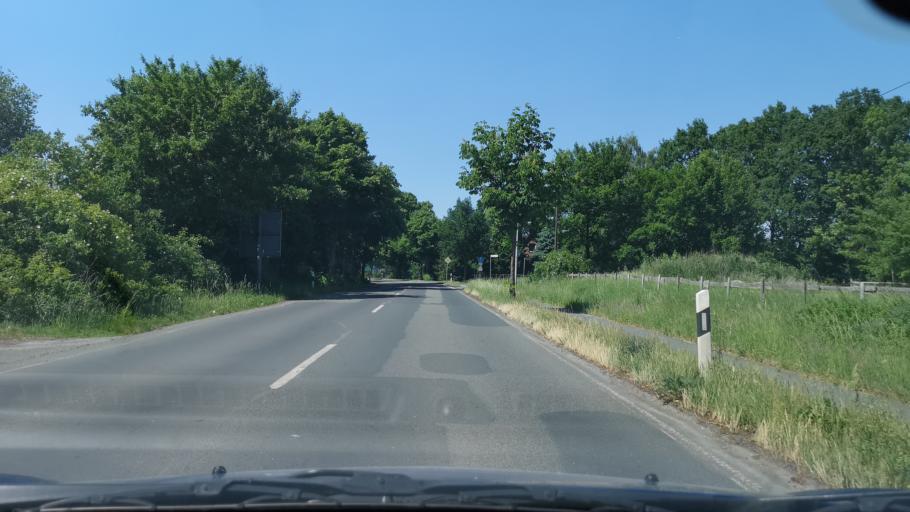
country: DE
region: Lower Saxony
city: Garbsen-Mitte
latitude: 52.4451
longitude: 9.6392
